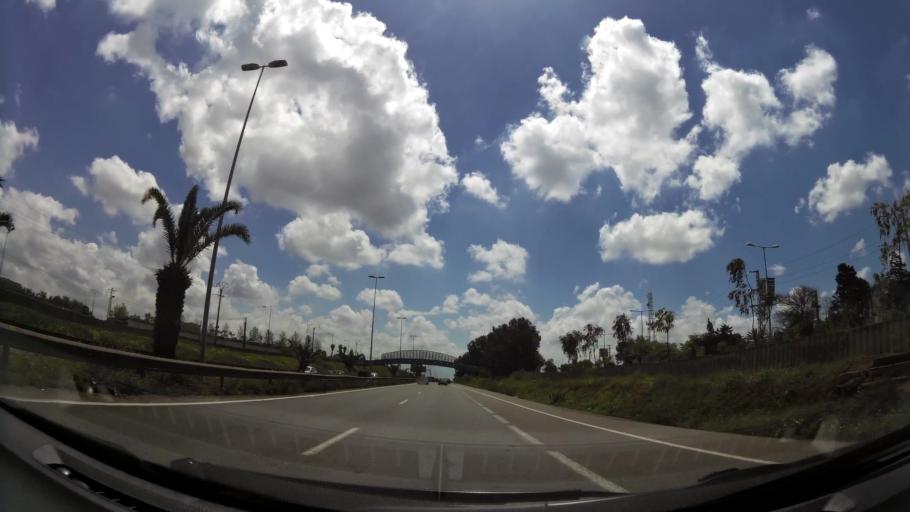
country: MA
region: Grand Casablanca
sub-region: Nouaceur
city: Bouskoura
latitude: 33.4954
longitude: -7.6291
